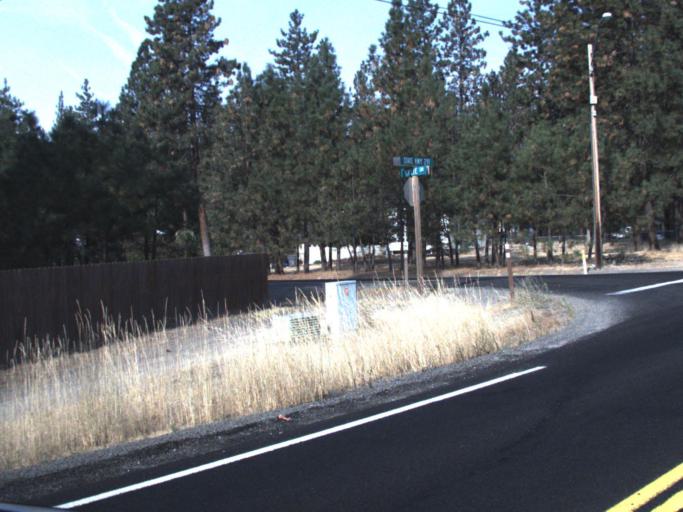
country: US
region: Washington
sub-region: Spokane County
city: Deer Park
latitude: 47.8205
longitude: -117.5863
